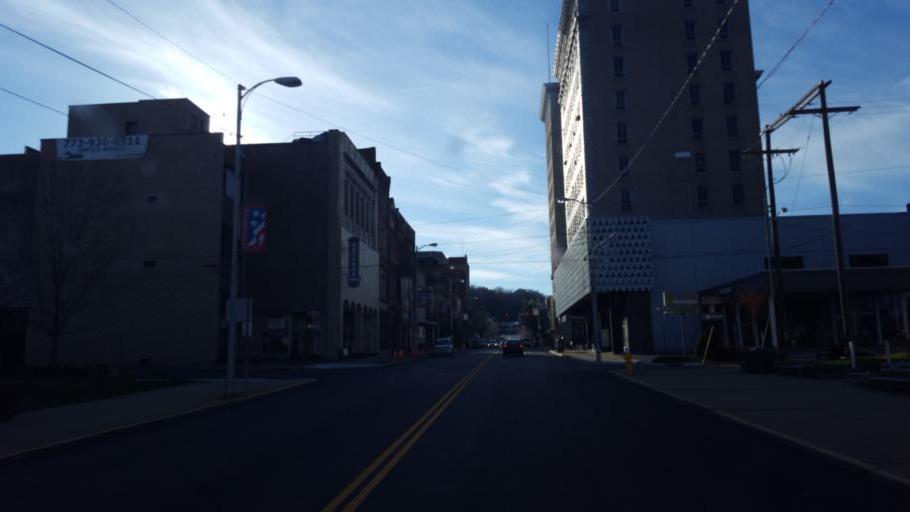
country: US
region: Ohio
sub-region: Jefferson County
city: Steubenville
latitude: 40.3597
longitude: -80.6139
